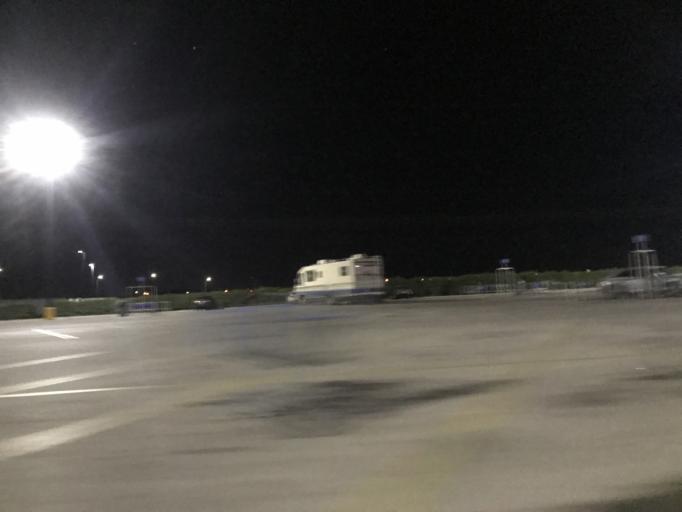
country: US
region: Texas
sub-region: Taylor County
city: Abilene
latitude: 32.4798
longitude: -99.6988
